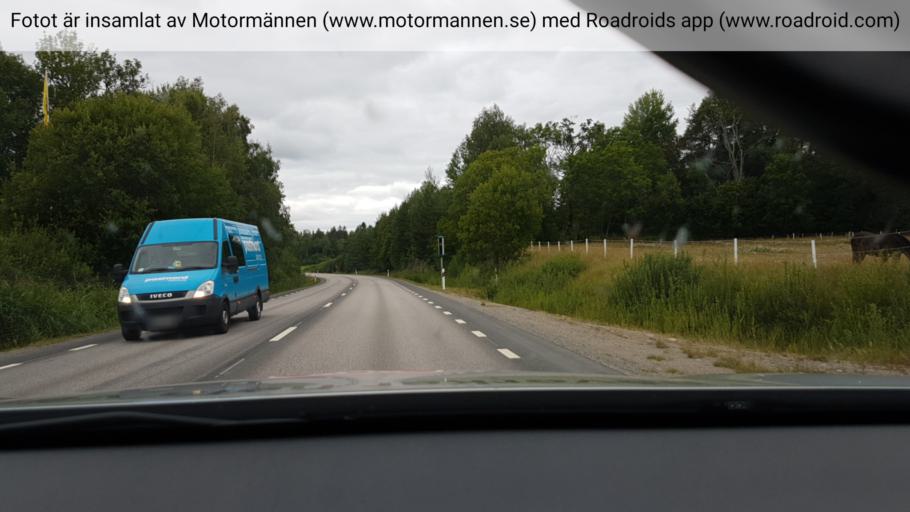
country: SE
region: Stockholm
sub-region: Nynashamns Kommun
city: Osmo
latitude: 58.9823
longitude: 17.8765
